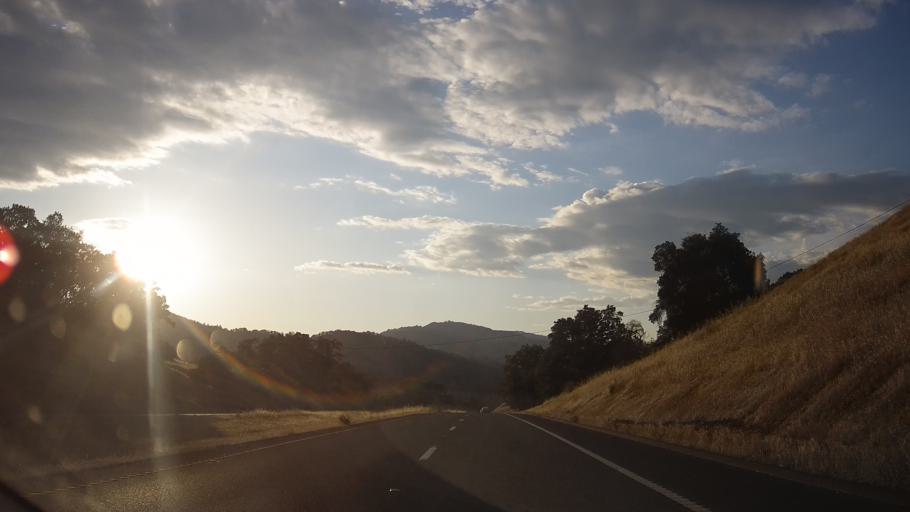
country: US
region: California
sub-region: Mendocino County
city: Talmage
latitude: 39.0736
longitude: -123.1733
